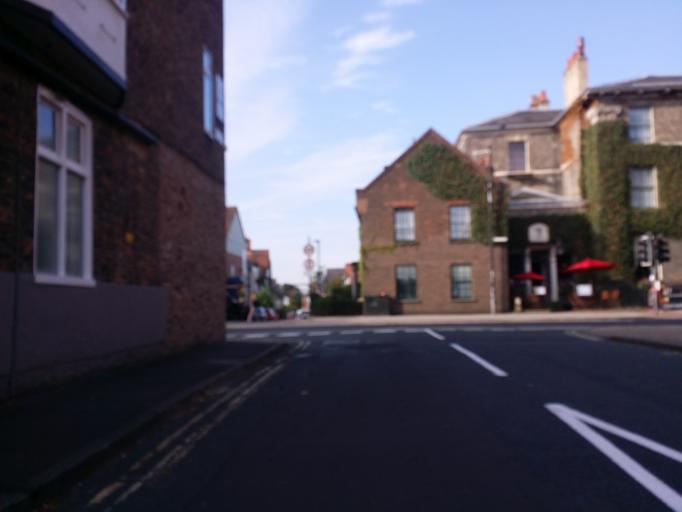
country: GB
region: England
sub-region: City of York
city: York
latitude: 53.9660
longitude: -1.0905
